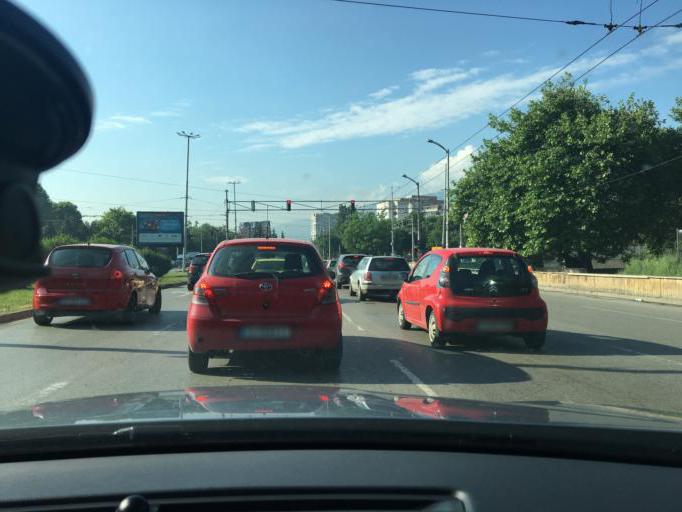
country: BG
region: Sofia-Capital
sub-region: Stolichna Obshtina
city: Sofia
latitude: 42.6802
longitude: 23.3021
